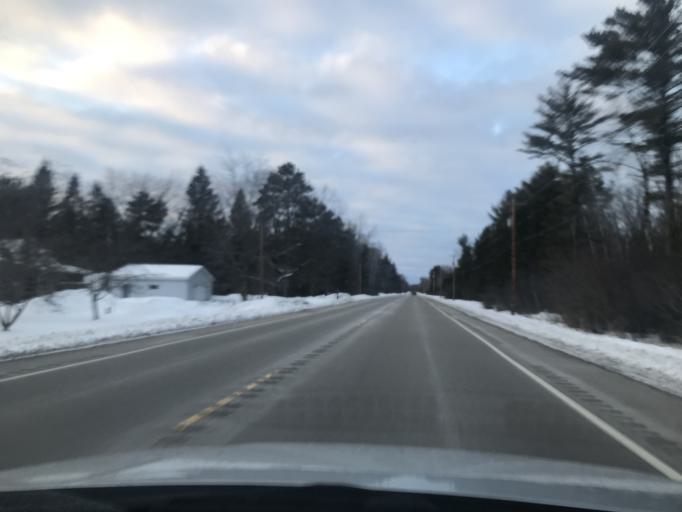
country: US
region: Wisconsin
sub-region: Marinette County
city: Marinette
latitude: 45.1450
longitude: -87.6973
